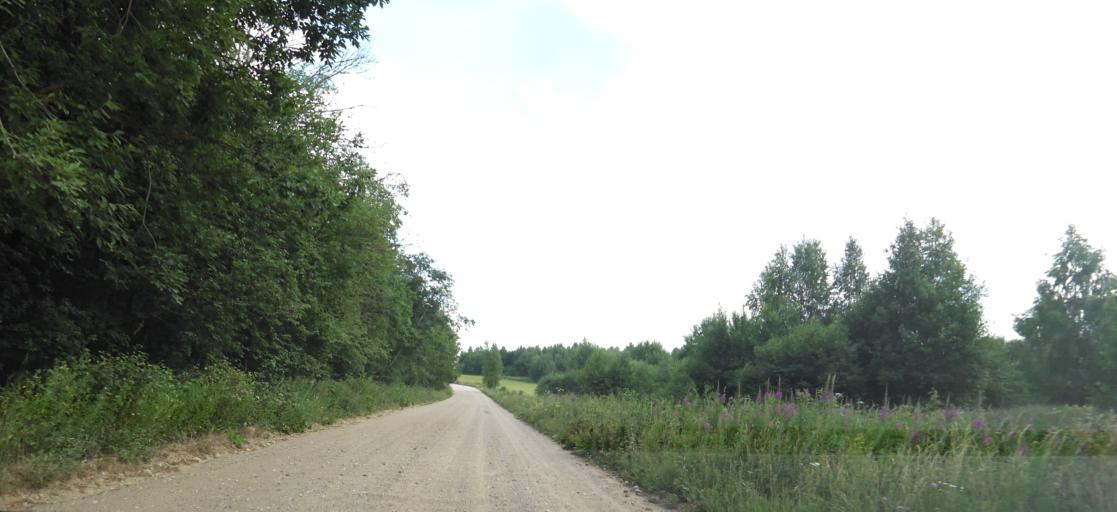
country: LT
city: Skaidiskes
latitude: 54.5321
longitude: 25.6308
